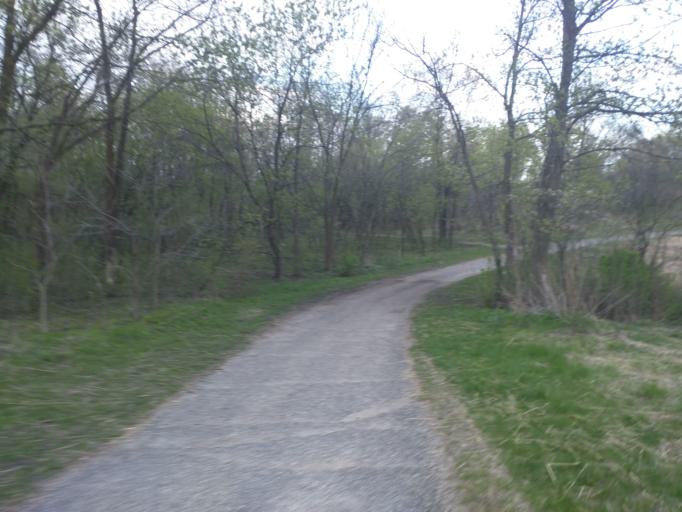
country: US
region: Minnesota
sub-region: Hennepin County
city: Minnetonka
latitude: 44.9012
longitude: -93.4986
